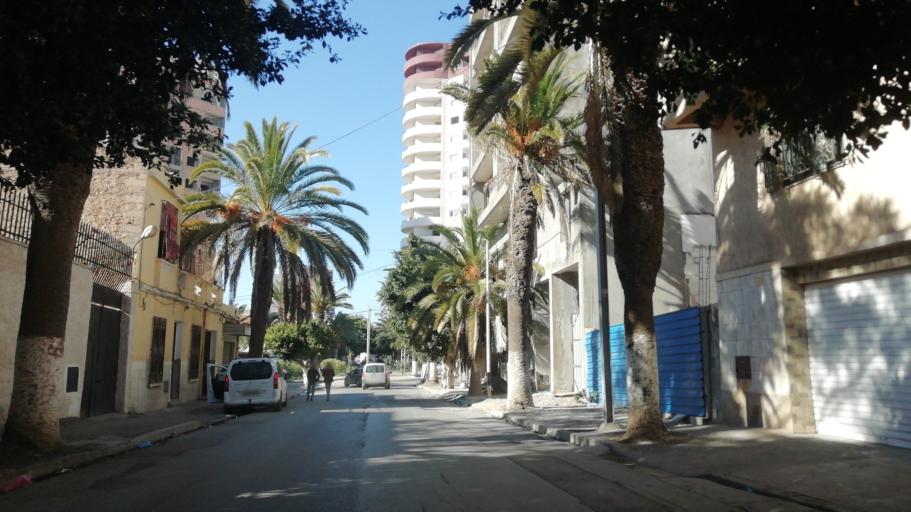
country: DZ
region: Oran
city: Oran
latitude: 35.7096
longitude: -0.6159
